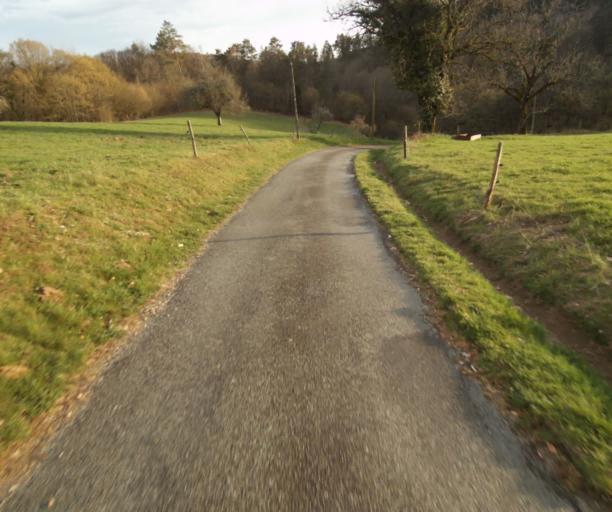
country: FR
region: Limousin
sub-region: Departement de la Correze
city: Argentat
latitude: 45.2160
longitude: 1.9787
